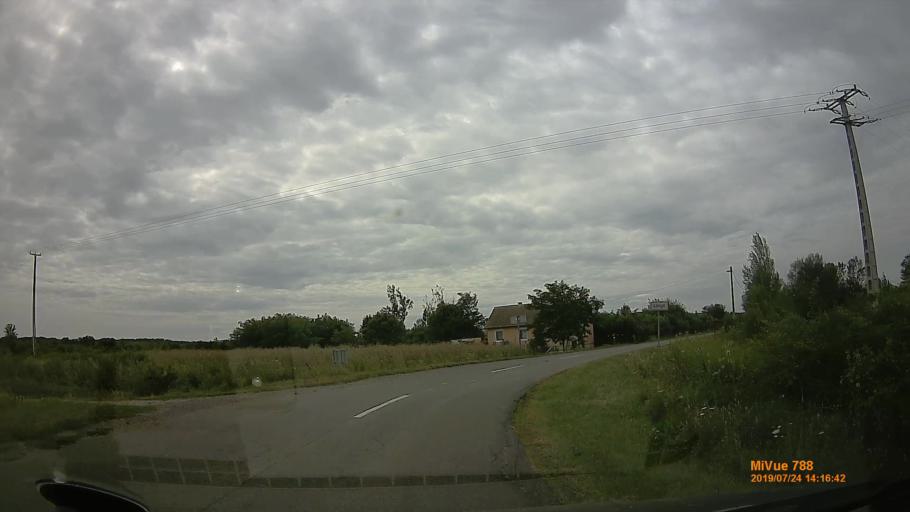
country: HU
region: Szabolcs-Szatmar-Bereg
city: Mandok
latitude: 48.3145
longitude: 22.2914
